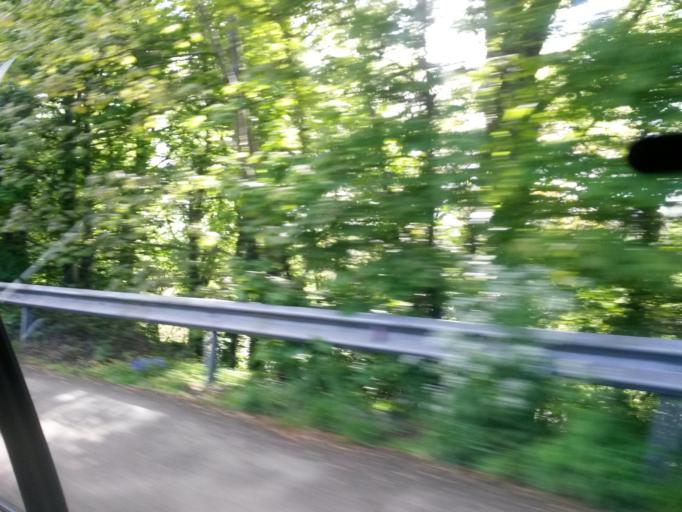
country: IE
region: Leinster
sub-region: Loch Garman
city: Enniscorthy
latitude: 52.5094
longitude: -6.5667
